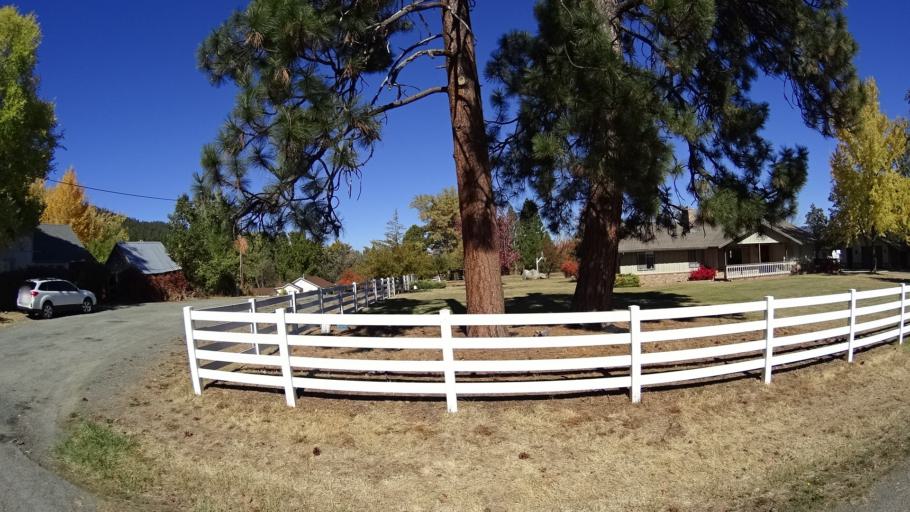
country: US
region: California
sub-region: Siskiyou County
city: Yreka
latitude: 41.4557
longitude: -122.9003
